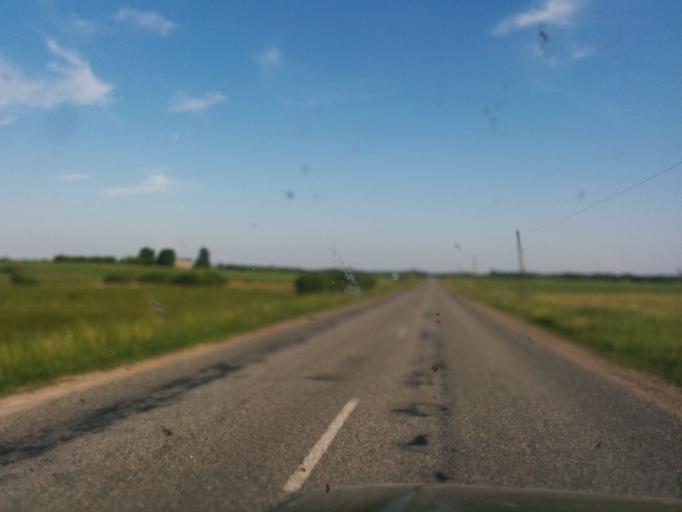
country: LV
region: Talsu Rajons
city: Valdemarpils
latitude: 57.3383
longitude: 22.5091
